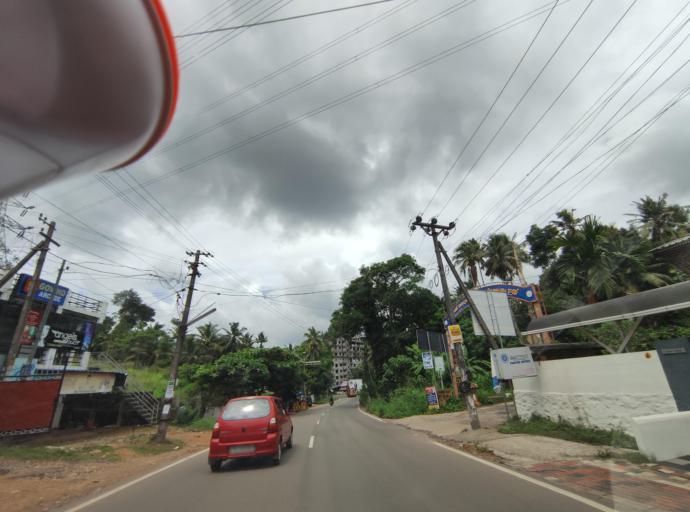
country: IN
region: Kerala
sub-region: Thiruvananthapuram
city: Nedumangad
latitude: 8.5767
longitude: 76.9433
